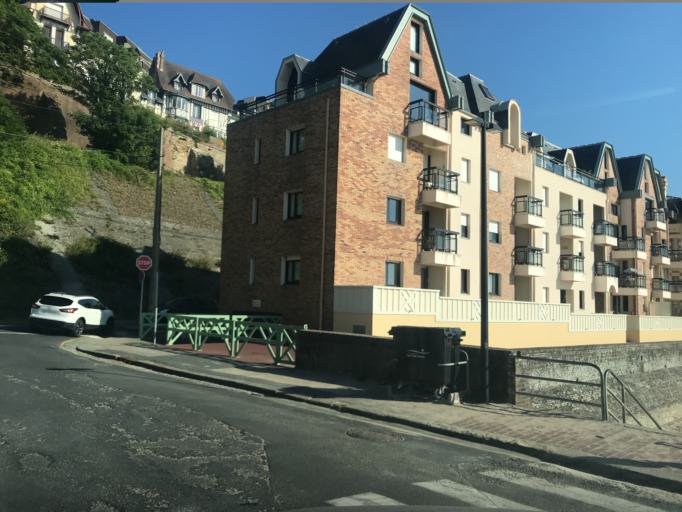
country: FR
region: Lower Normandy
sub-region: Departement du Calvados
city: Trouville-sur-Mer
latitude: 49.3746
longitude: 0.0855
